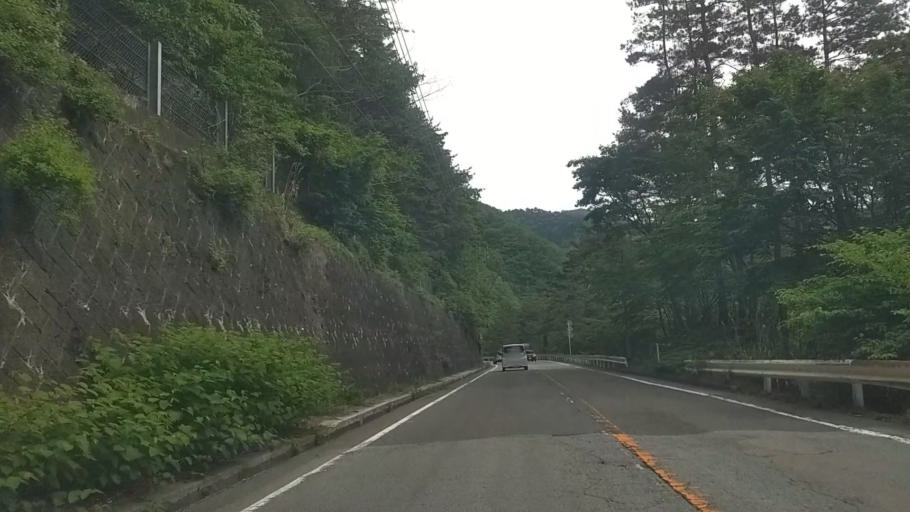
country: JP
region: Yamanashi
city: Fujikawaguchiko
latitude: 35.5198
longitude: 138.6182
